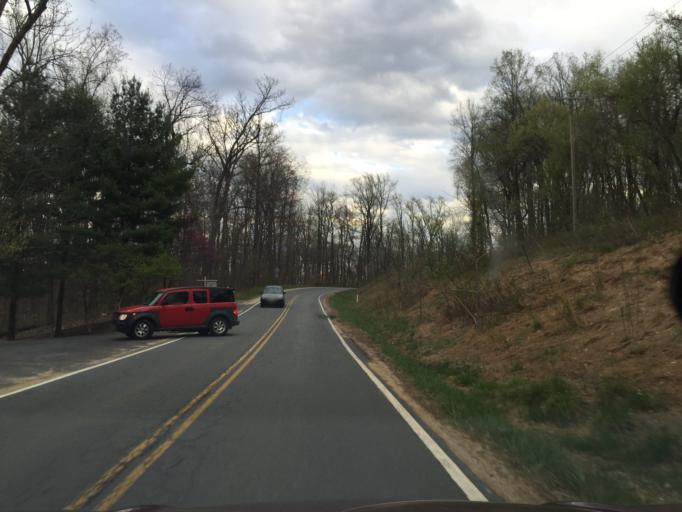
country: US
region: Maryland
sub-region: Frederick County
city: Point of Rocks
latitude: 39.2454
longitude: -77.5603
